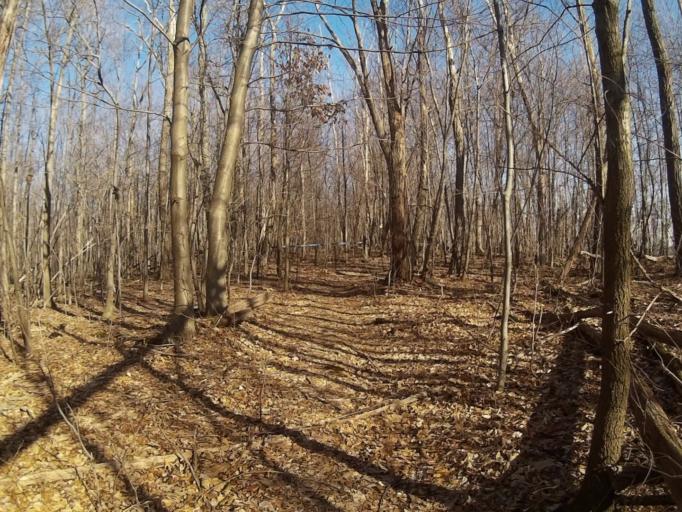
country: US
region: Pennsylvania
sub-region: Centre County
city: Boalsburg
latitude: 40.8104
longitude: -77.7804
